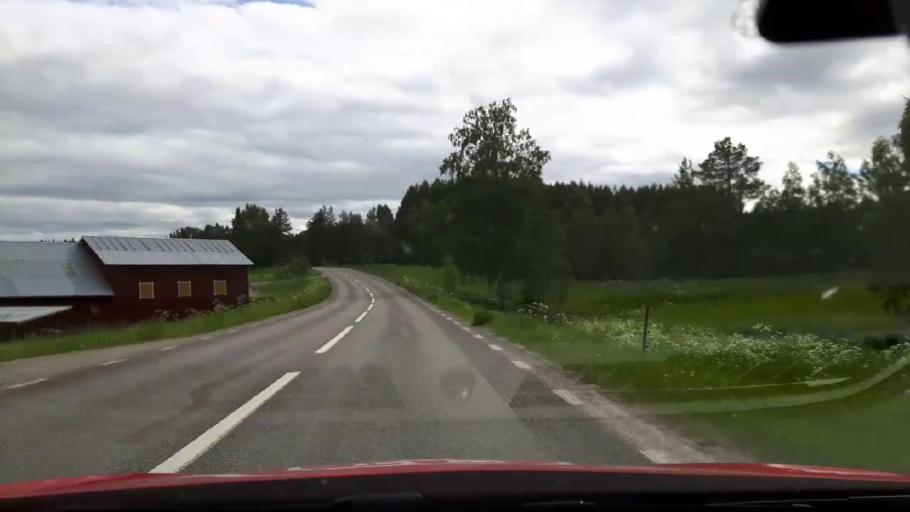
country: SE
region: Jaemtland
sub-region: Ragunda Kommun
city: Hammarstrand
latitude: 63.0954
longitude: 16.3571
